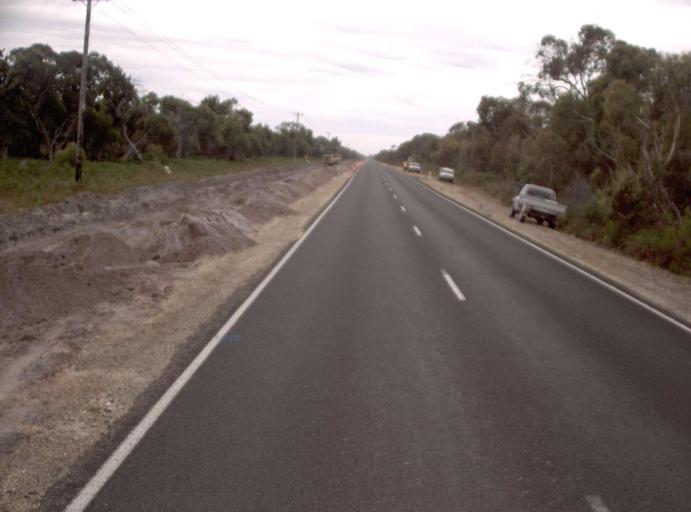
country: AU
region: Victoria
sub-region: East Gippsland
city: Bairnsdale
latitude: -38.0761
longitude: 147.5403
